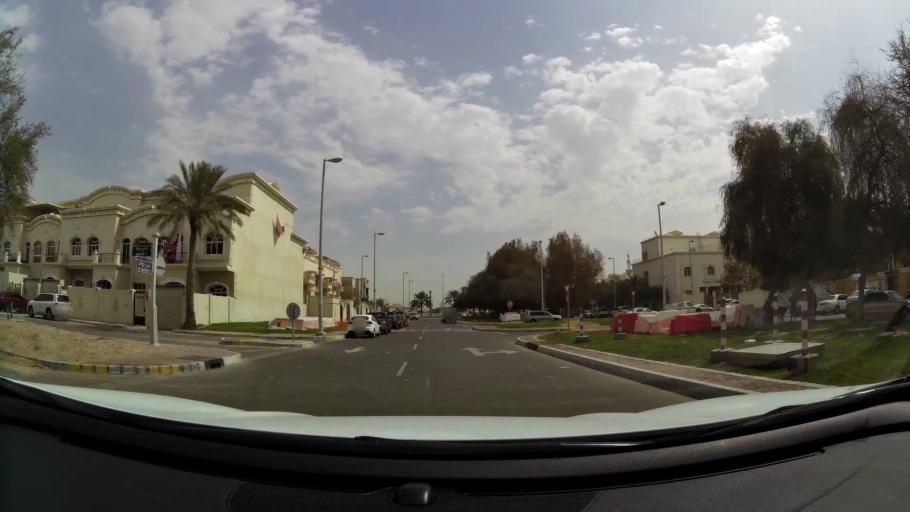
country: AE
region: Abu Dhabi
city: Abu Dhabi
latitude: 24.4623
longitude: 54.3406
